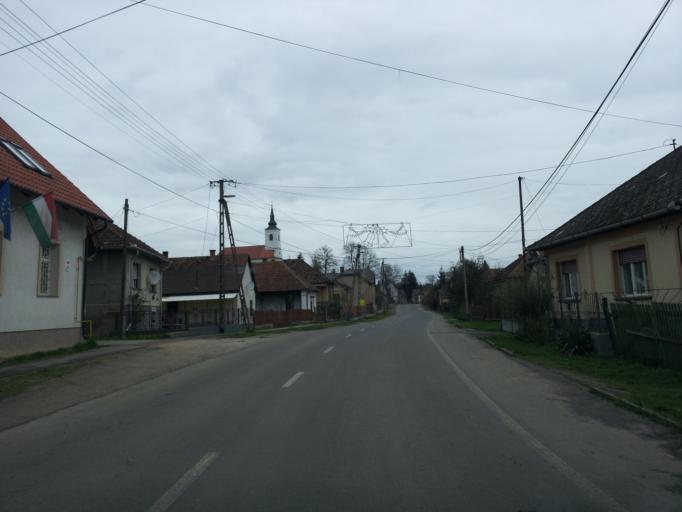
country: HU
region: Borsod-Abauj-Zemplen
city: Rudabanya
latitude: 48.4973
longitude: 20.6603
